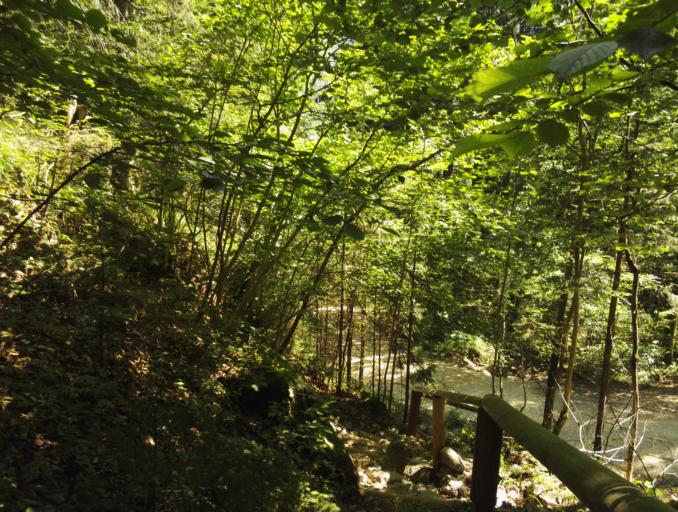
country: AT
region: Styria
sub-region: Politischer Bezirk Graz-Umgebung
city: Rothelstein
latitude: 47.3452
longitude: 15.3896
